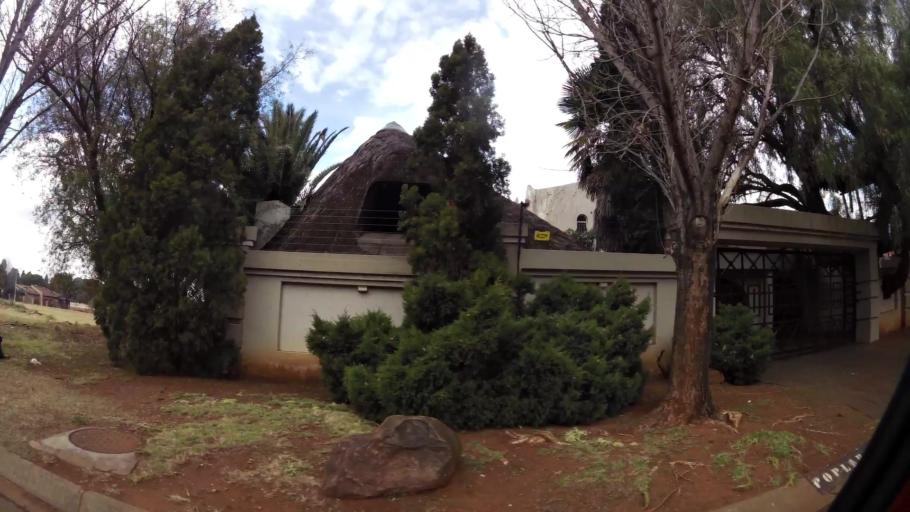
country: ZA
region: Gauteng
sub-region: Sedibeng District Municipality
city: Vanderbijlpark
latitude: -26.7401
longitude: 27.8506
